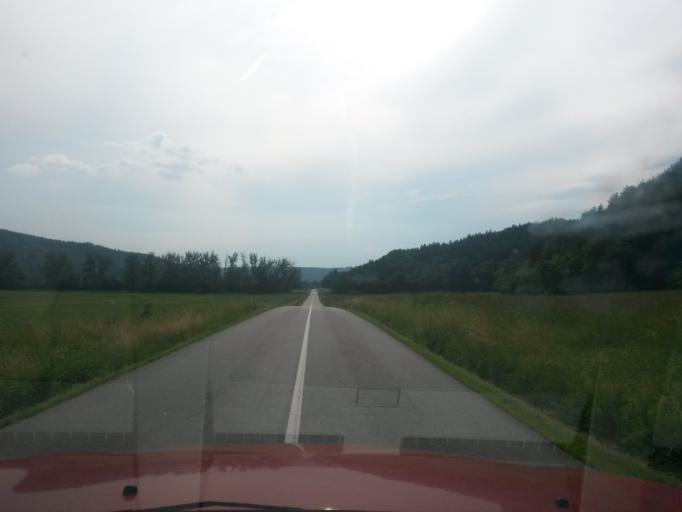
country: SK
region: Presovsky
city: Humenne
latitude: 48.9801
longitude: 21.9940
